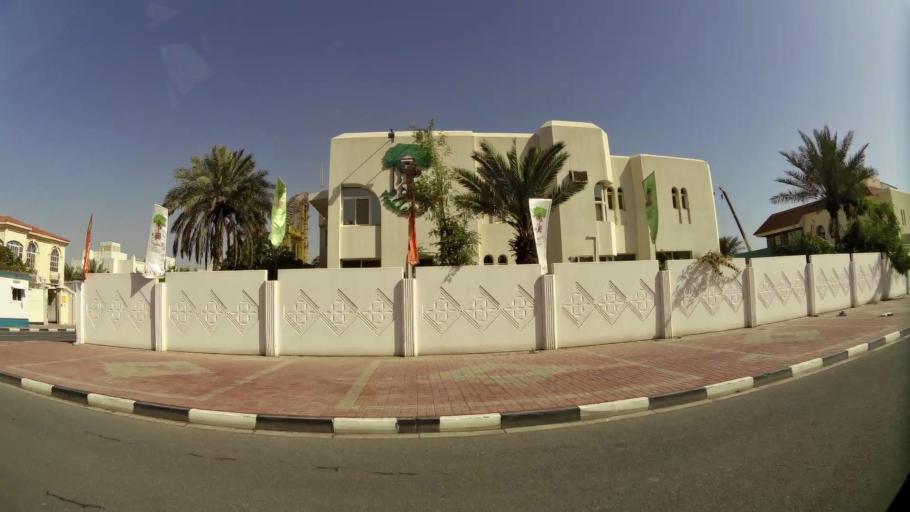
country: QA
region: Baladiyat ad Dawhah
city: Doha
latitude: 25.3319
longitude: 51.5187
